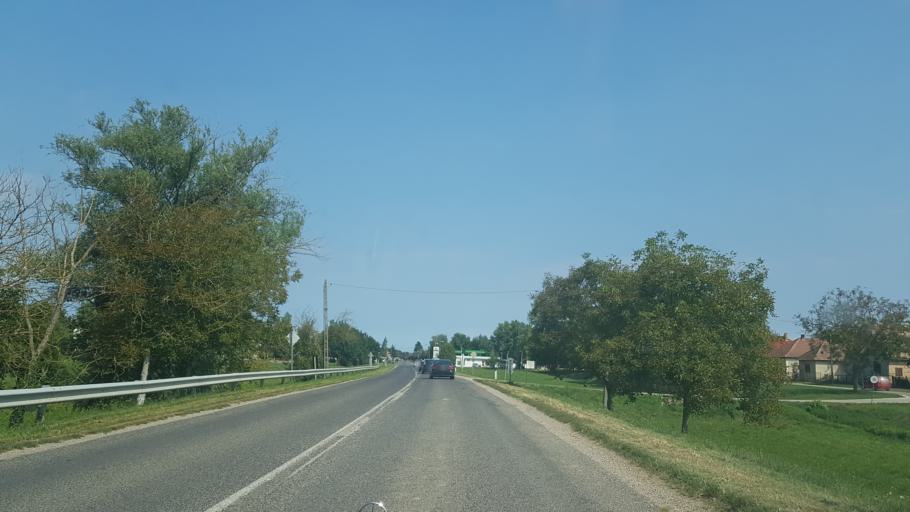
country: HU
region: Somogy
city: Segesd
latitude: 46.3397
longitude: 17.3486
